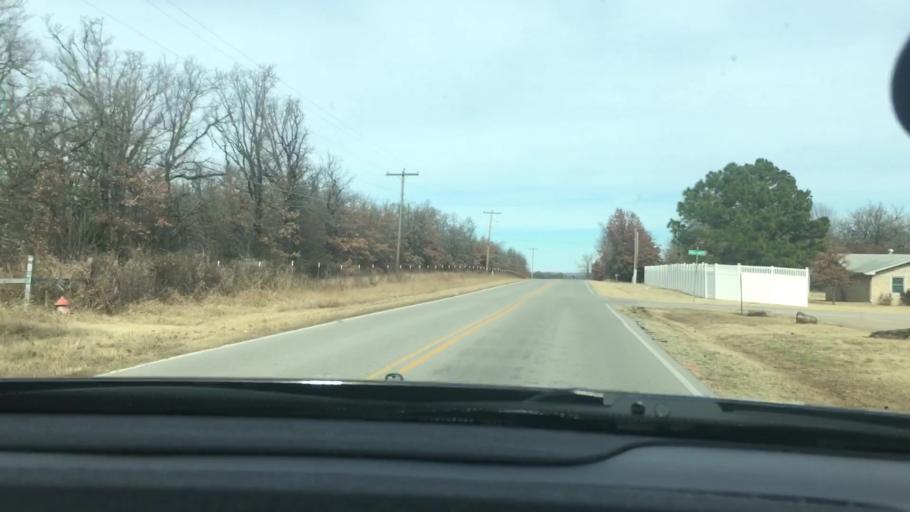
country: US
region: Oklahoma
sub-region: Carter County
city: Ardmore
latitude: 34.1771
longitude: -97.0731
